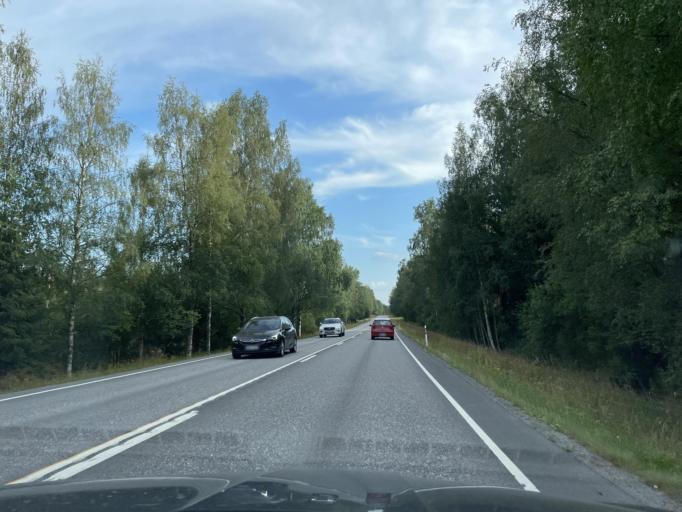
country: FI
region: Paijanne Tavastia
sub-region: Lahti
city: Padasjoki
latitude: 61.4329
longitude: 25.1853
